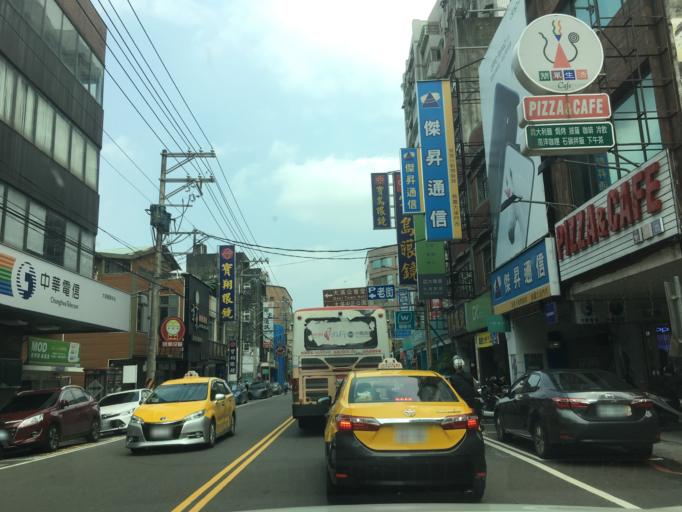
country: TW
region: Taiwan
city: Daxi
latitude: 24.8817
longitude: 121.2889
